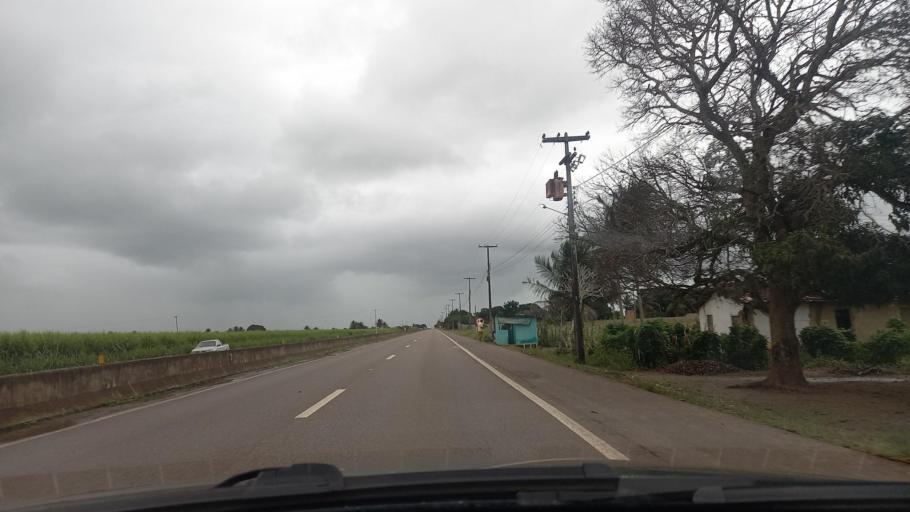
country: BR
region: Alagoas
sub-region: Limoeiro De Anadia
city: Cajueiro
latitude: -9.7584
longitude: -36.4407
